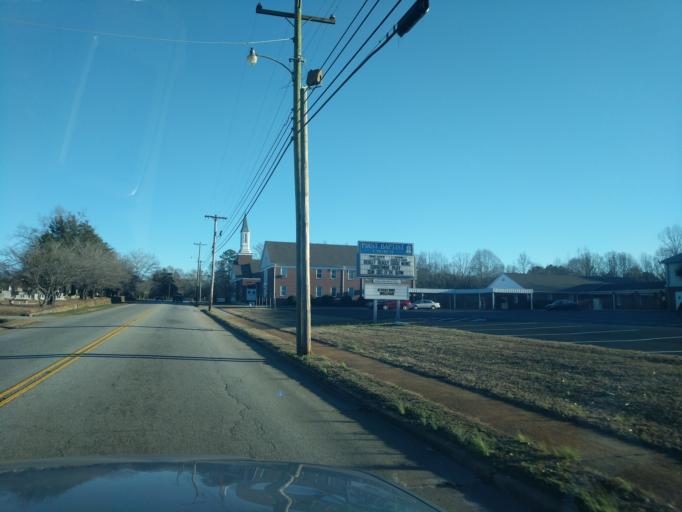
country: US
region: South Carolina
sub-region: Oconee County
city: Westminster
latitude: 34.6560
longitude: -83.0873
